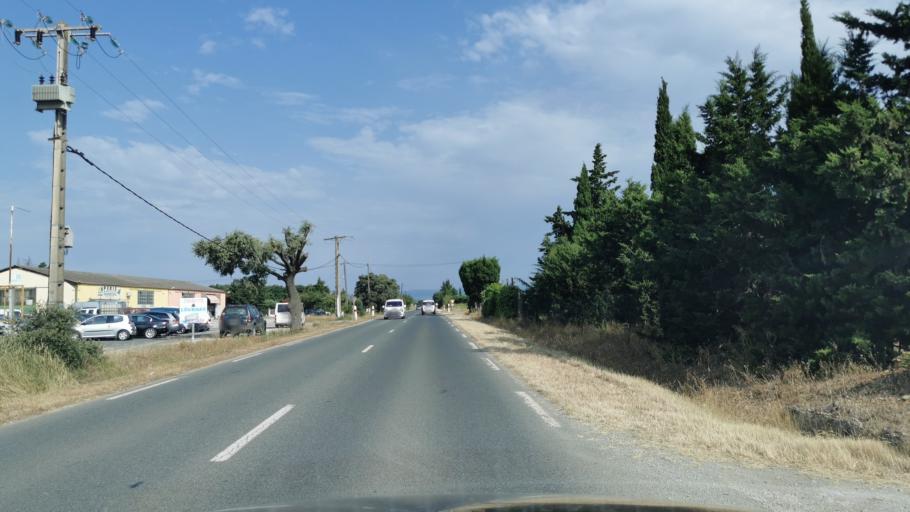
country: FR
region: Languedoc-Roussillon
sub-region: Departement de l'Aude
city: Ginestas
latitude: 43.2653
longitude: 2.9007
